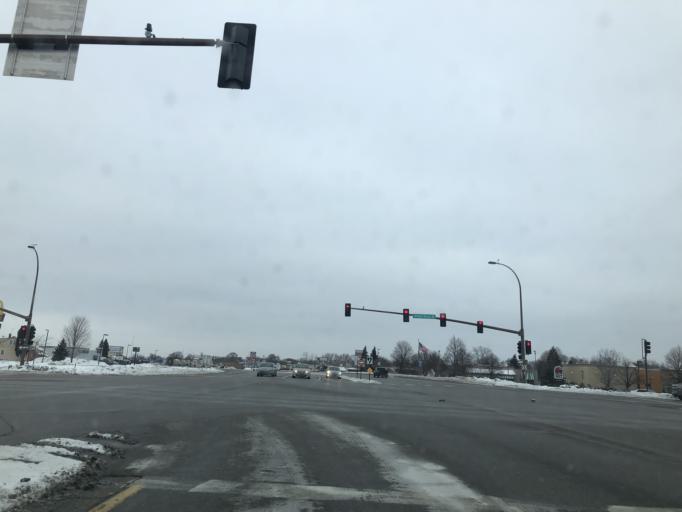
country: US
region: Minnesota
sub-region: Hennepin County
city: Osseo
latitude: 45.1086
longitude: -93.3945
